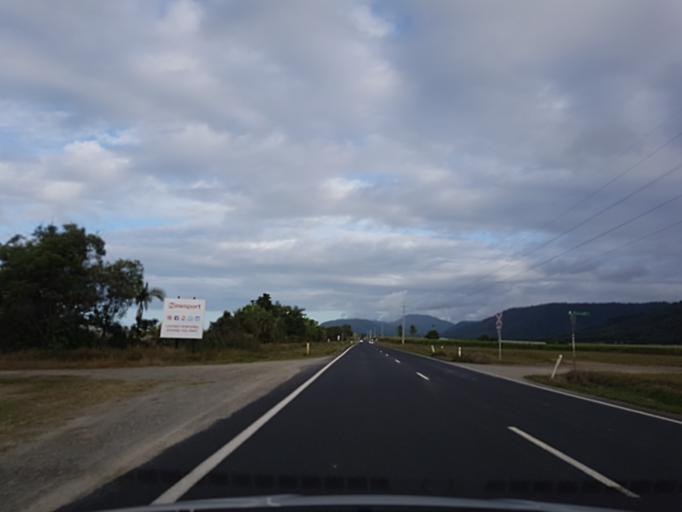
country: AU
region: Queensland
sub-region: Cairns
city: Port Douglas
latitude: -16.5101
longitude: 145.4428
